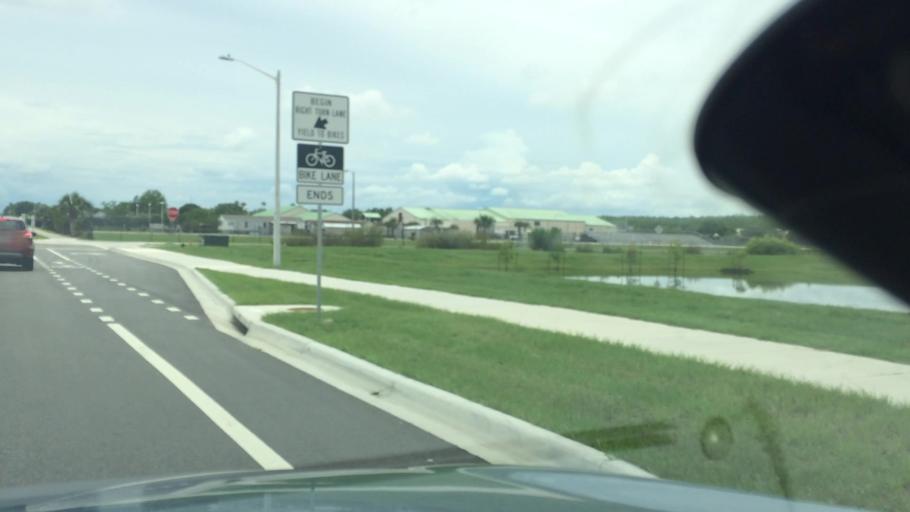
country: US
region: Florida
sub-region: Osceola County
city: Kissimmee
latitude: 28.3199
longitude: -81.4366
